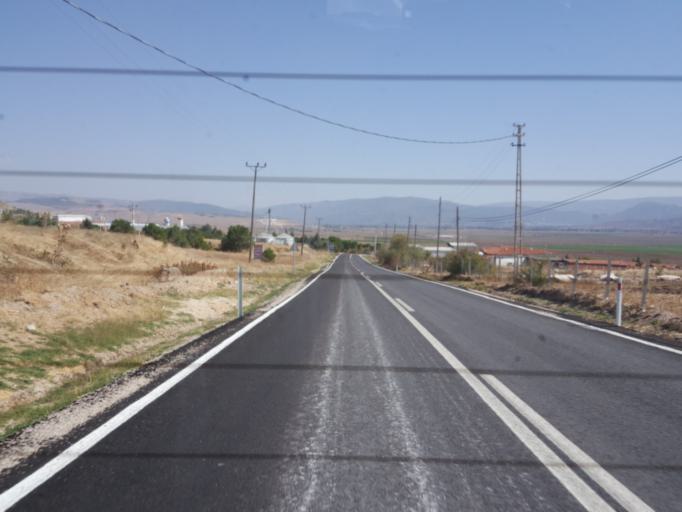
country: TR
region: Amasya
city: Dogantepe
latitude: 40.5823
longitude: 35.6345
